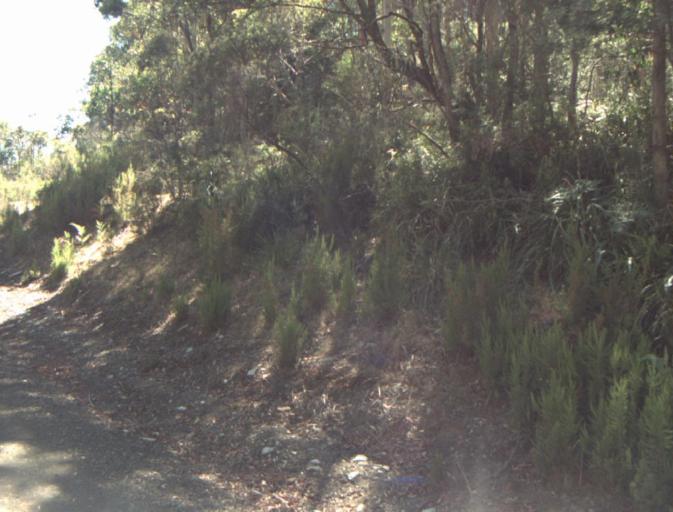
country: AU
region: Tasmania
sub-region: Launceston
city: Newstead
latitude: -41.3024
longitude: 147.3341
